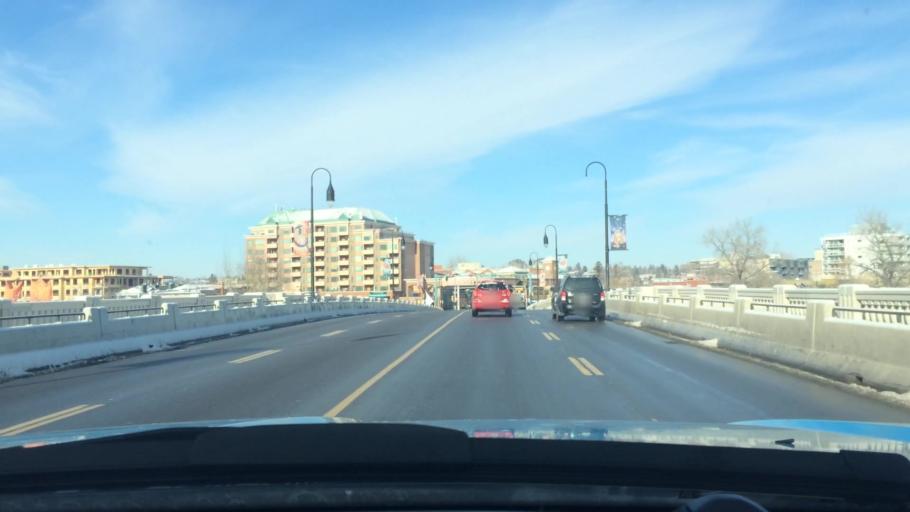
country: CA
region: Alberta
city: Calgary
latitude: 51.0506
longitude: -114.0842
